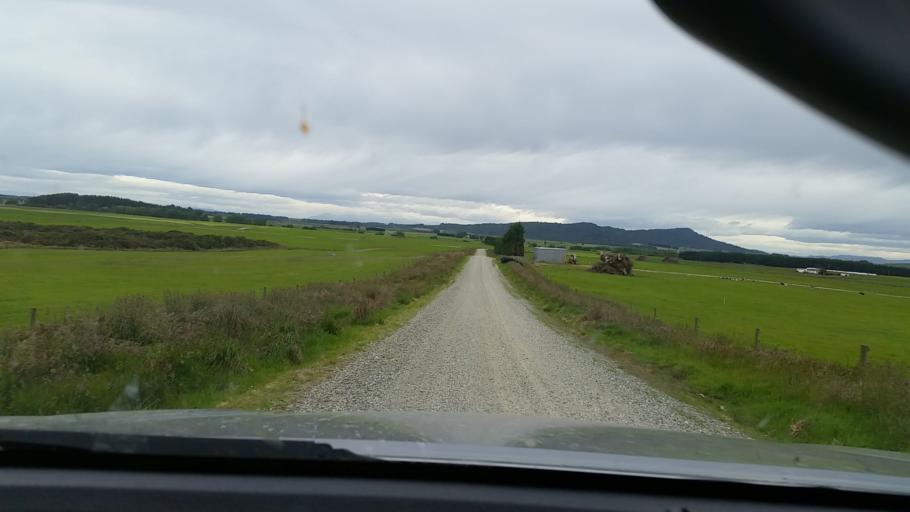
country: NZ
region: Southland
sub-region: Invercargill City
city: Invercargill
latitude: -46.2731
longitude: 168.4710
